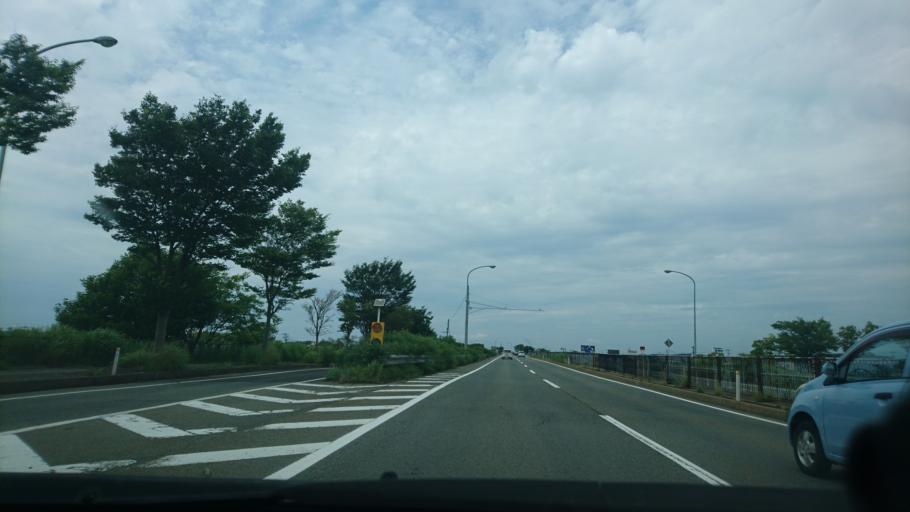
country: JP
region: Akita
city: Akita
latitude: 39.6741
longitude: 140.1531
